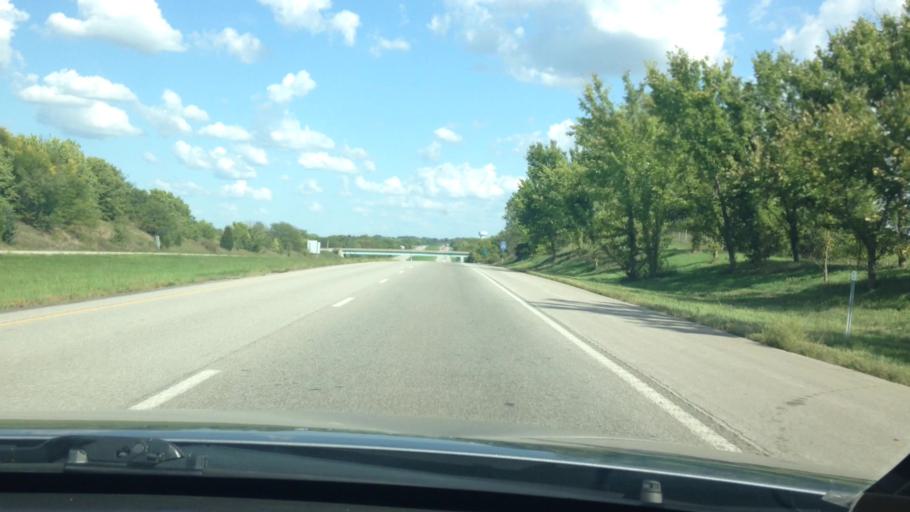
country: US
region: Missouri
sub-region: Clay County
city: Smithville
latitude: 39.3110
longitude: -94.5490
